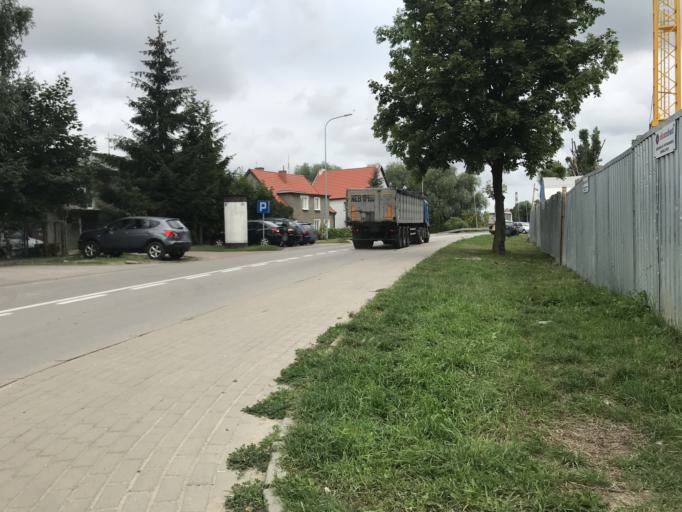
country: PL
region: Warmian-Masurian Voivodeship
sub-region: Powiat elblaski
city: Elblag
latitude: 54.1632
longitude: 19.3894
